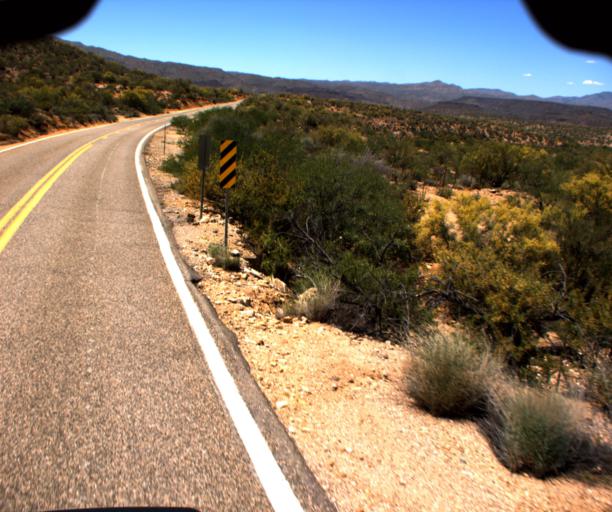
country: US
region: Arizona
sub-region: Yavapai County
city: Bagdad
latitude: 34.4603
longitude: -113.0385
